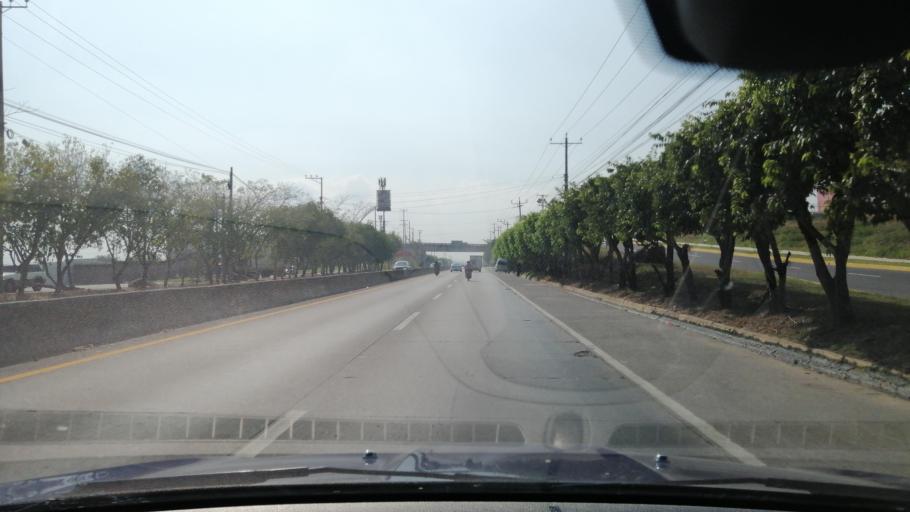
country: SV
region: San Salvador
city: Apopa
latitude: 13.7988
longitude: -89.2306
